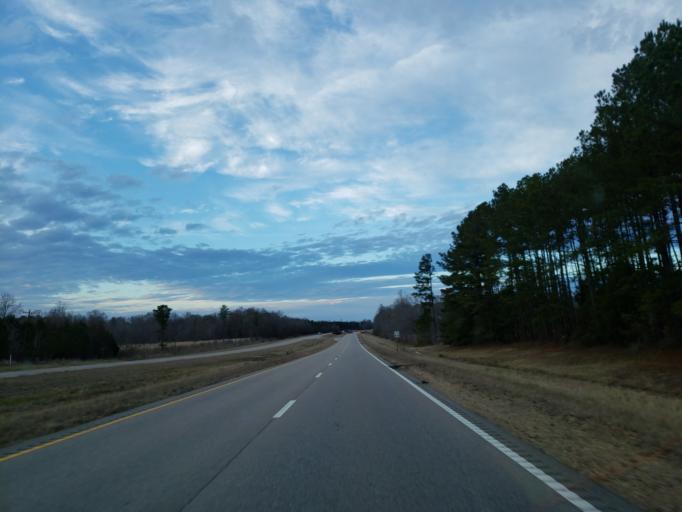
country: US
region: Mississippi
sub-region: Kemper County
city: De Kalb
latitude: 32.7515
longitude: -88.4658
